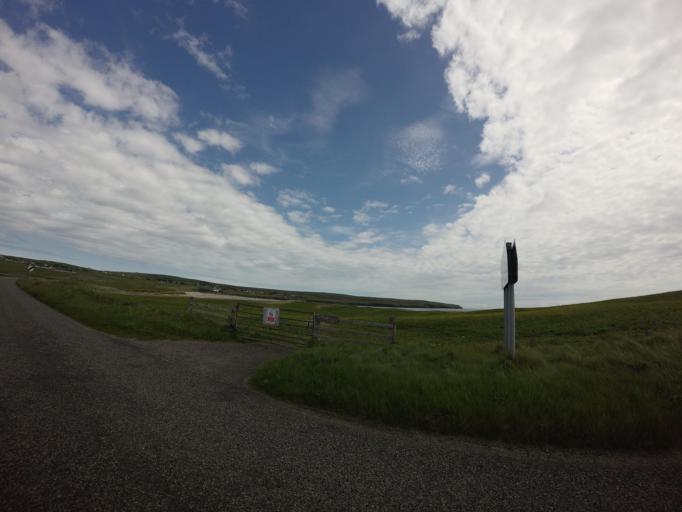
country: GB
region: Scotland
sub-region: Eilean Siar
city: Isle of Lewis
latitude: 58.2860
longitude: -6.2832
